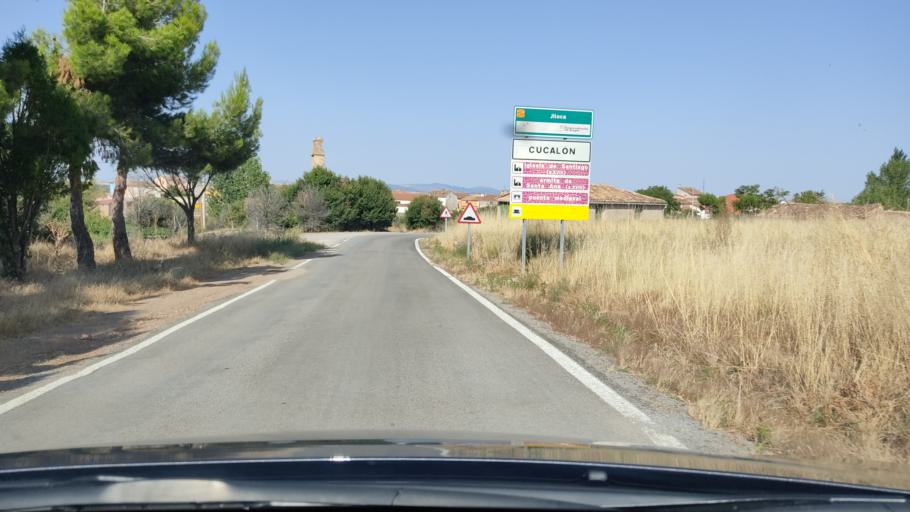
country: ES
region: Aragon
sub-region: Provincia de Teruel
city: Cucalon
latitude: 41.0861
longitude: -1.2112
